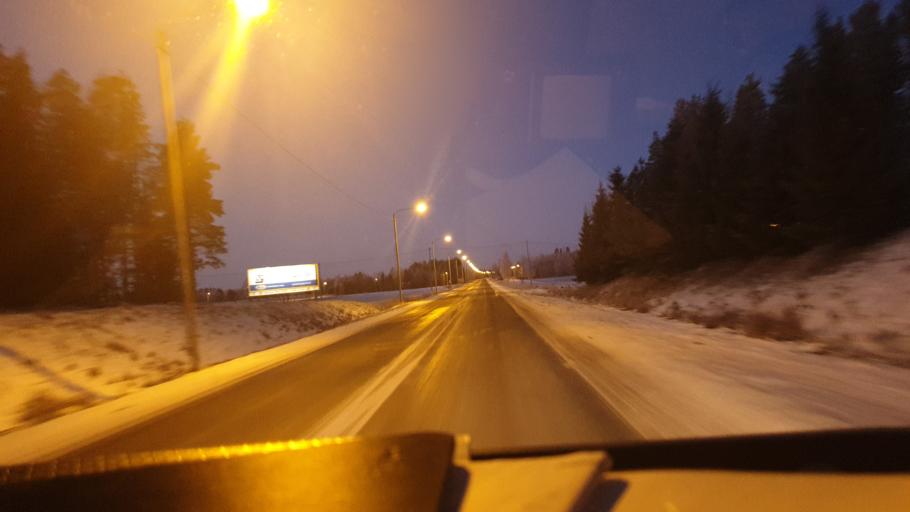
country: FI
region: Northern Ostrobothnia
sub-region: Raahe
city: Raahe
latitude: 64.6893
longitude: 24.6167
